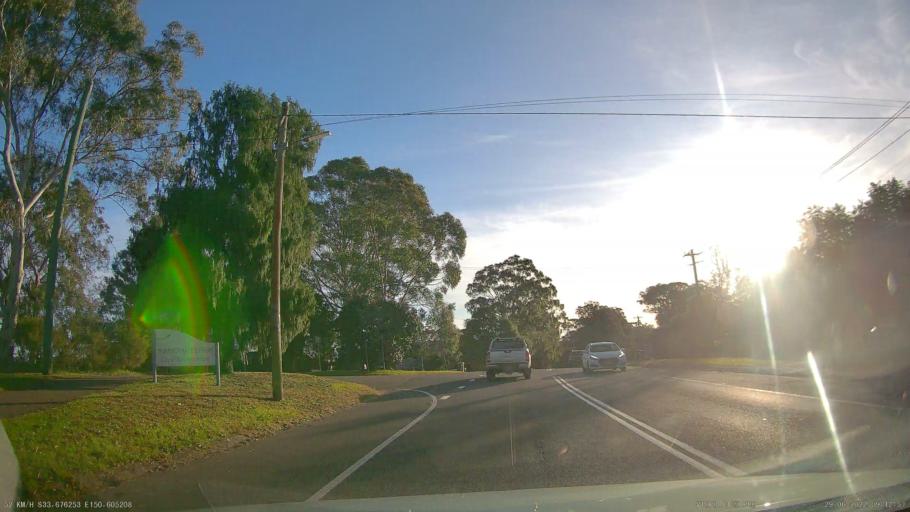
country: AU
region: New South Wales
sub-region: Penrith Municipality
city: Emu Heights
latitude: -33.6759
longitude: 150.6053
